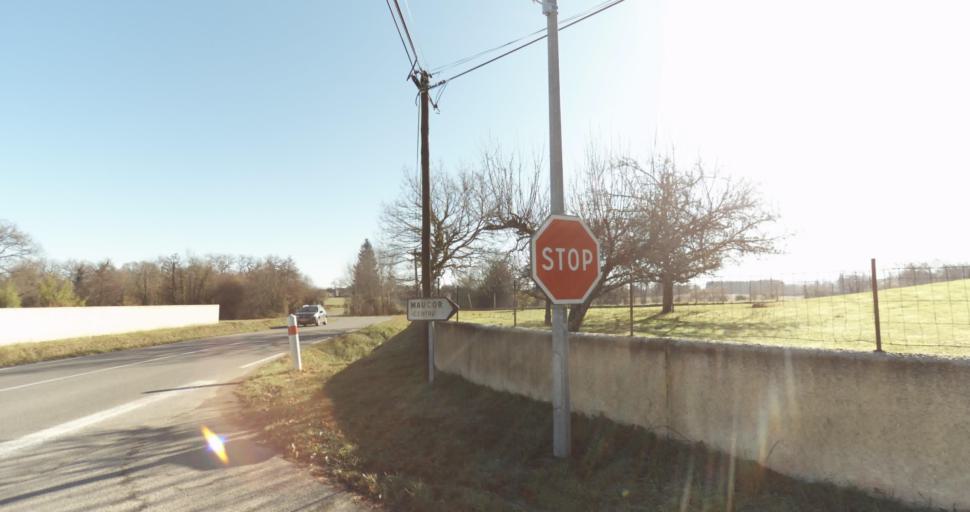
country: FR
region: Aquitaine
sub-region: Departement des Pyrenees-Atlantiques
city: Morlaas
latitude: 43.3548
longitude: -0.2707
